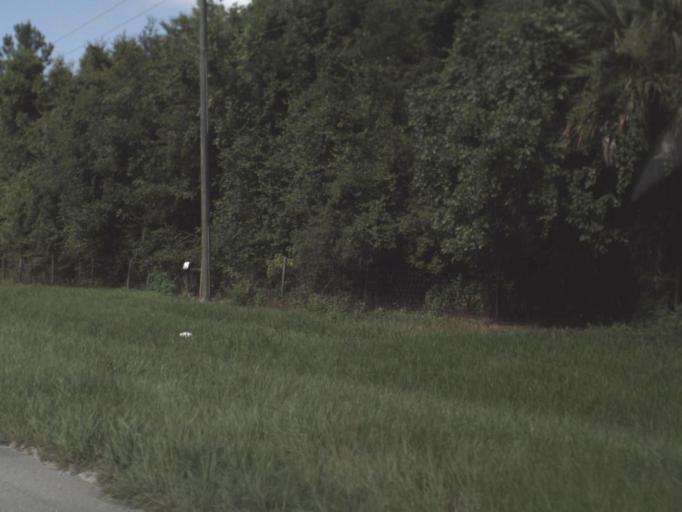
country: US
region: Florida
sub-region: Hernando County
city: North Brooksville
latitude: 28.5679
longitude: -82.4210
